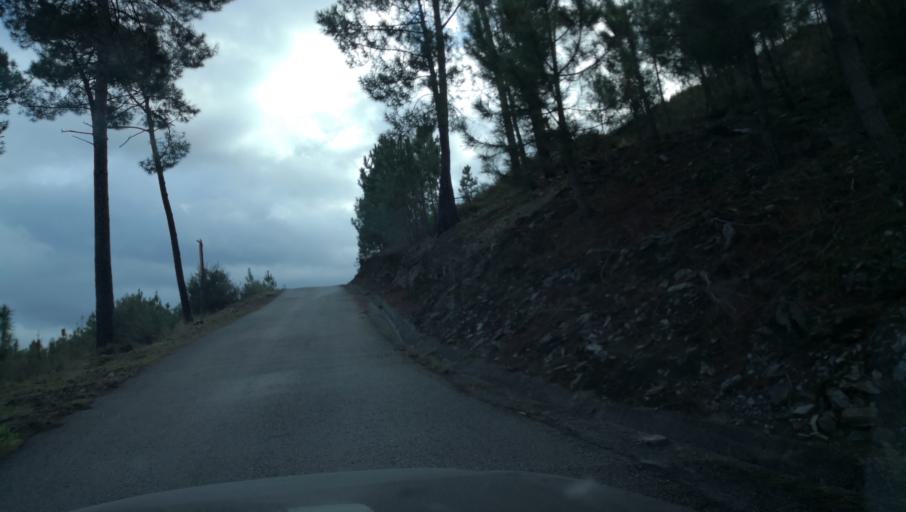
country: PT
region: Vila Real
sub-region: Sabrosa
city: Vilela
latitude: 41.2004
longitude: -7.5787
